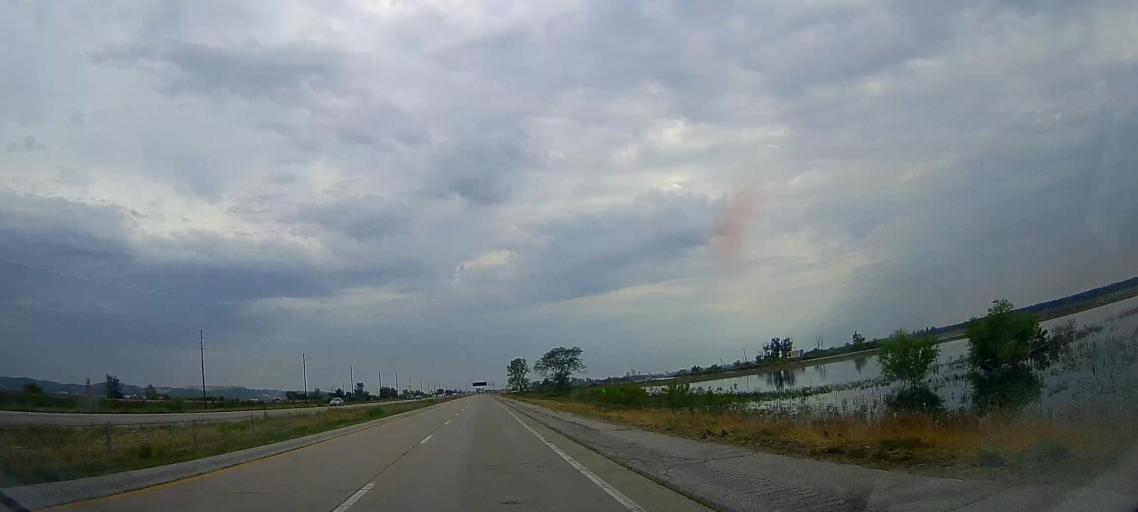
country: US
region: Iowa
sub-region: Pottawattamie County
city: Carter Lake
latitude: 41.3873
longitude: -95.8997
